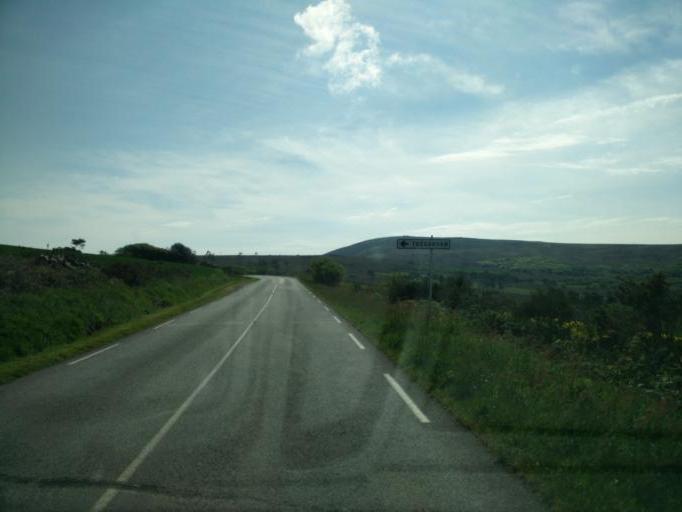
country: FR
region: Brittany
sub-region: Departement du Finistere
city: Plomodiern
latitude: 48.2245
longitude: -4.2579
